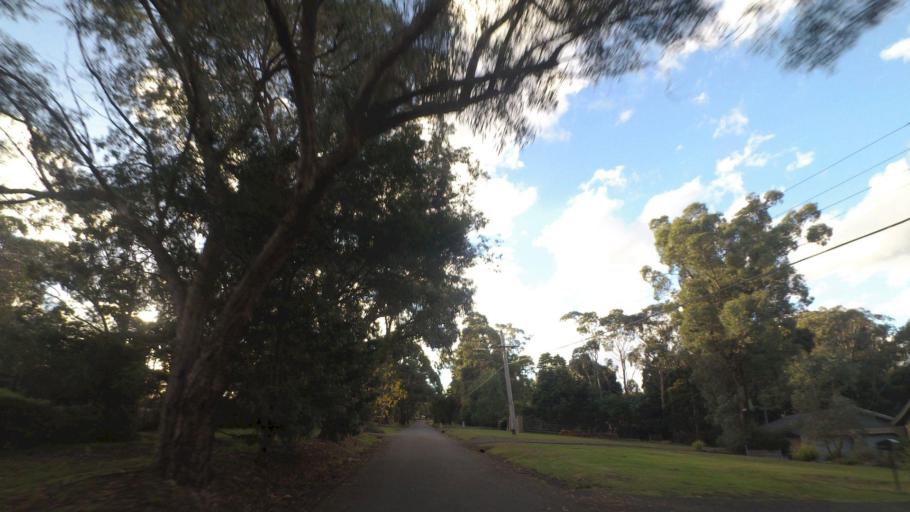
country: AU
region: Victoria
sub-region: Banyule
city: Lower Plenty
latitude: -37.7360
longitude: 145.1273
